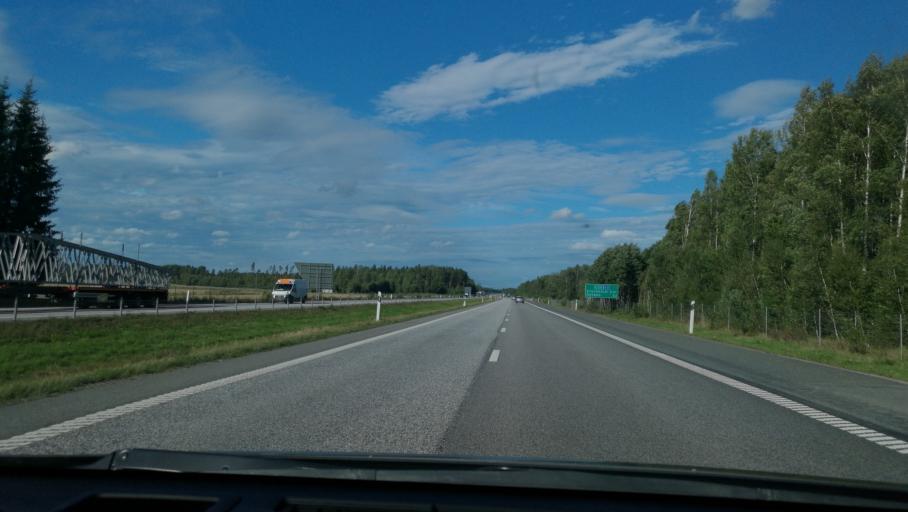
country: SE
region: OErebro
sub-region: Hallsbergs Kommun
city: Hallsberg
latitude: 59.1081
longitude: 15.0655
